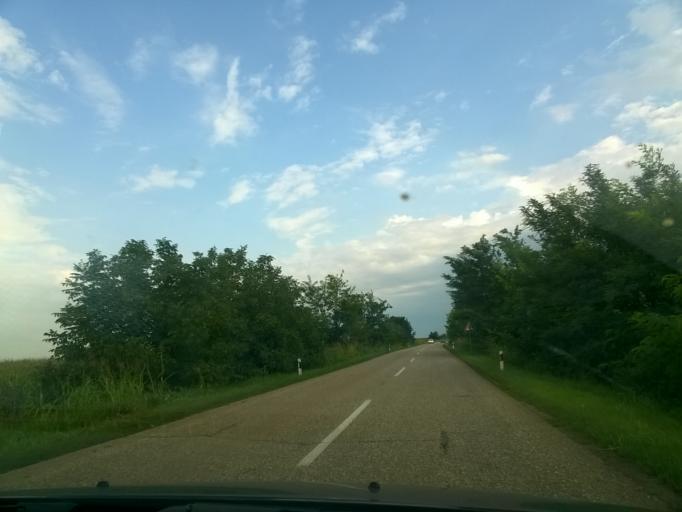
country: RS
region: Autonomna Pokrajina Vojvodina
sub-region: Juznobanatski Okrug
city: Kovacica
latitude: 45.1264
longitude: 20.6161
